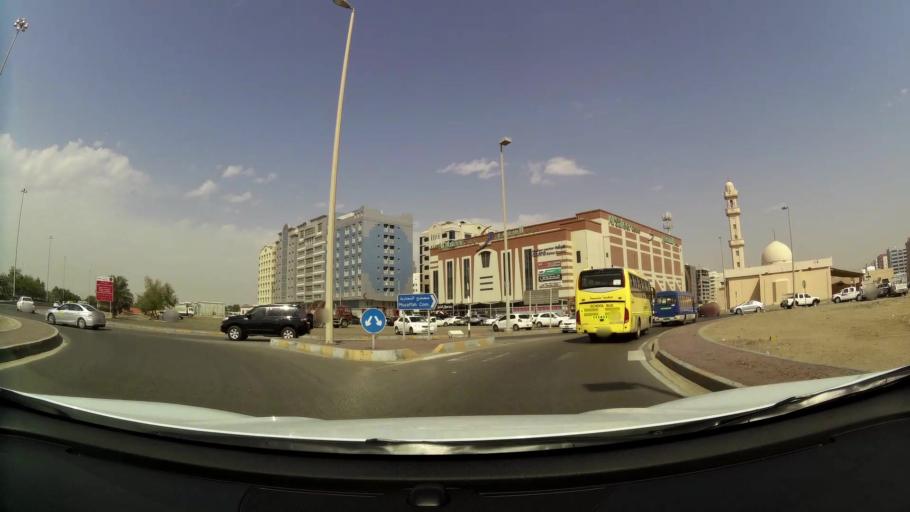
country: AE
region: Abu Dhabi
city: Abu Dhabi
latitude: 24.3422
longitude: 54.5295
